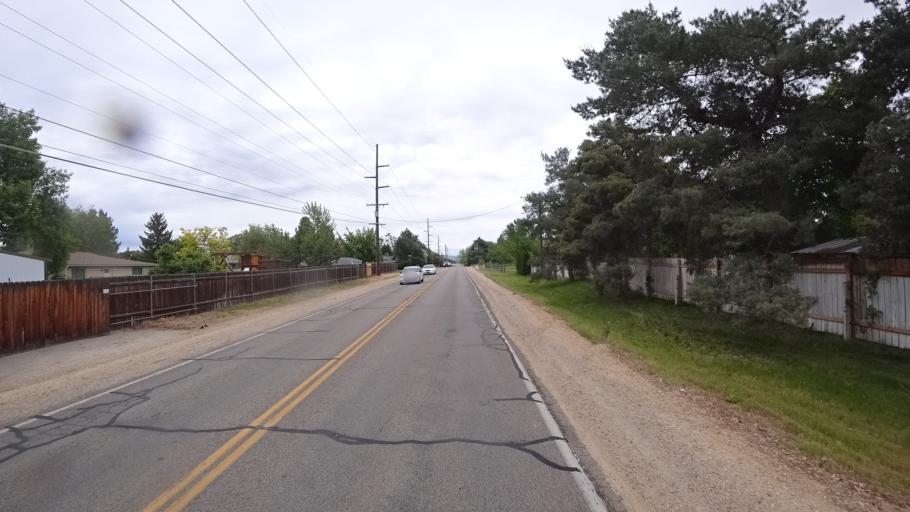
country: US
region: Idaho
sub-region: Ada County
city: Meridian
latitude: 43.5757
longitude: -116.3210
